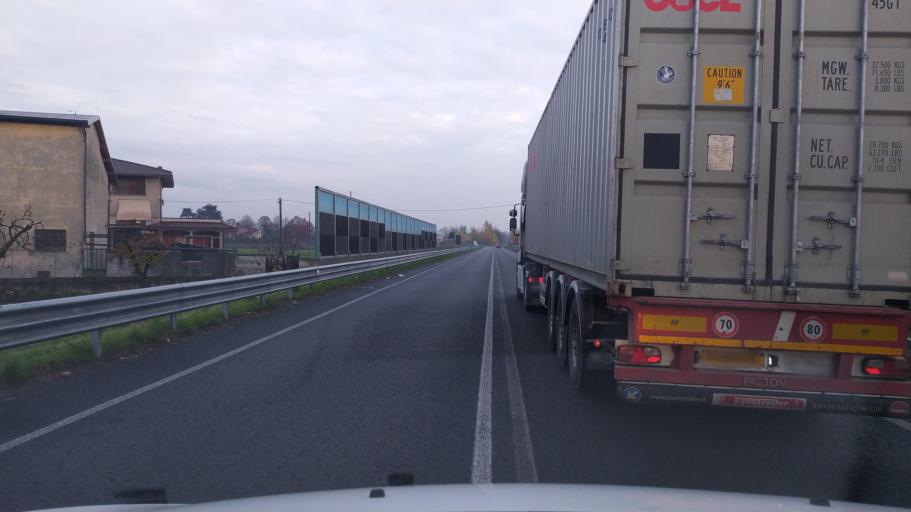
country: IT
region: Lombardy
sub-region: Provincia di Bergamo
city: Calcio
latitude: 45.5080
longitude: 9.8586
